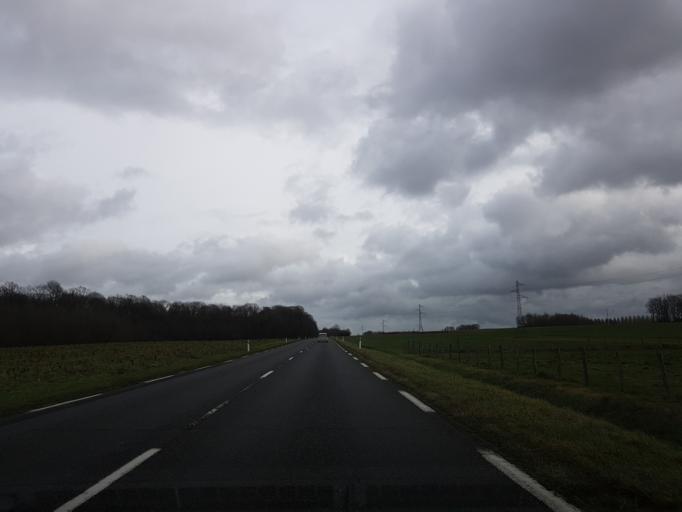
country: FR
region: Champagne-Ardenne
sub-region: Departement de la Haute-Marne
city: Fayl-Billot
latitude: 47.8126
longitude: 5.5169
